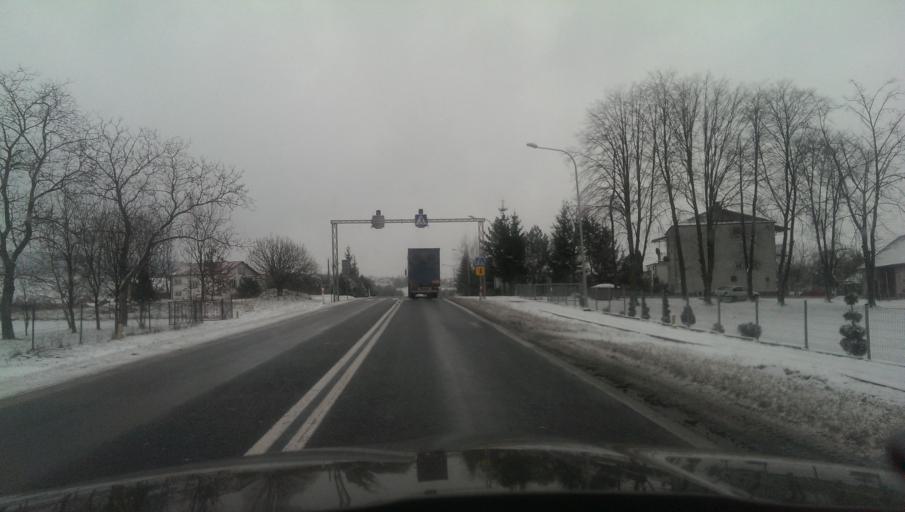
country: PL
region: Subcarpathian Voivodeship
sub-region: Powiat sanocki
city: Dlugie
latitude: 49.5767
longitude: 22.0483
